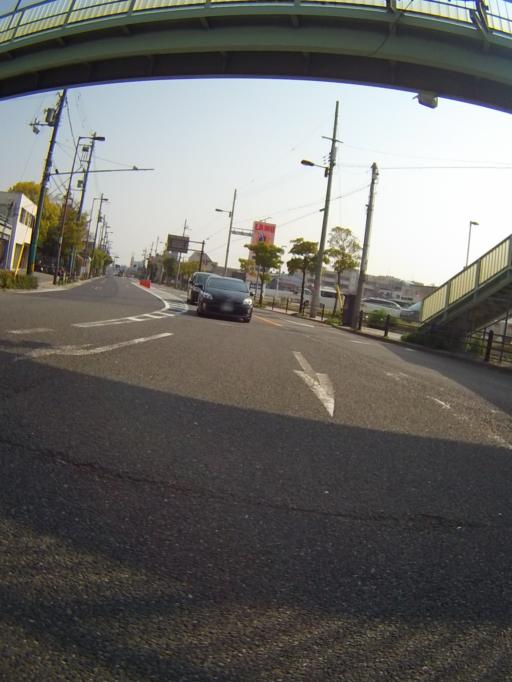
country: JP
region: Osaka
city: Osaka-shi
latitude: 34.6535
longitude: 135.4846
